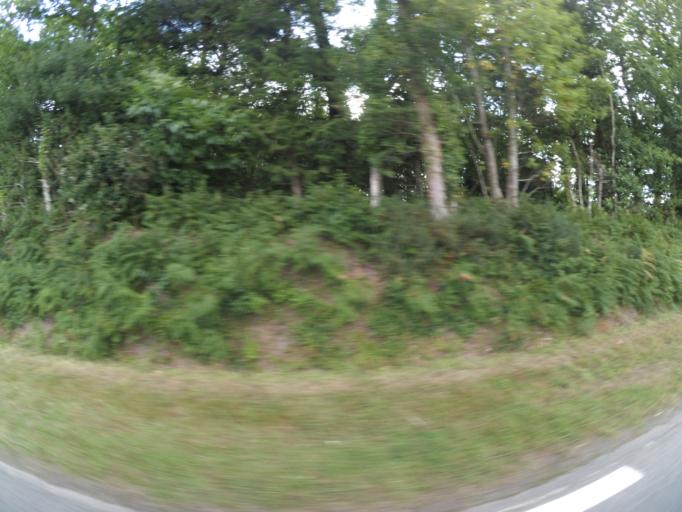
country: FR
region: Brittany
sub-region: Departement du Finistere
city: Redene
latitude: 47.8224
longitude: -3.4916
